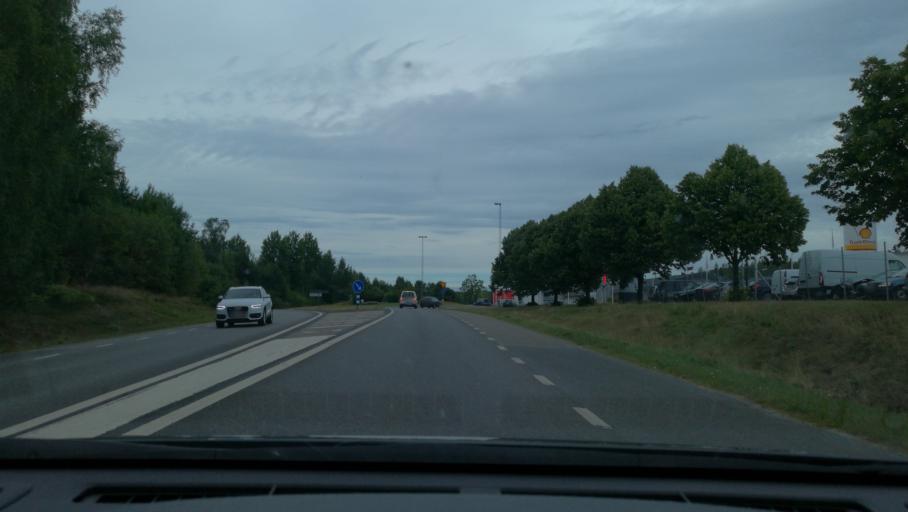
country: SE
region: Soedermanland
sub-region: Katrineholms Kommun
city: Katrineholm
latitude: 59.0007
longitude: 16.2220
